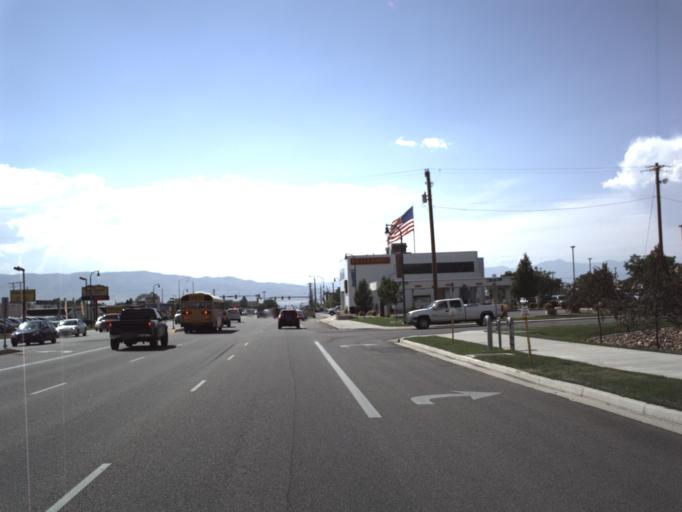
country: US
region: Utah
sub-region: Utah County
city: Orem
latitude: 40.3121
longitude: -111.6948
